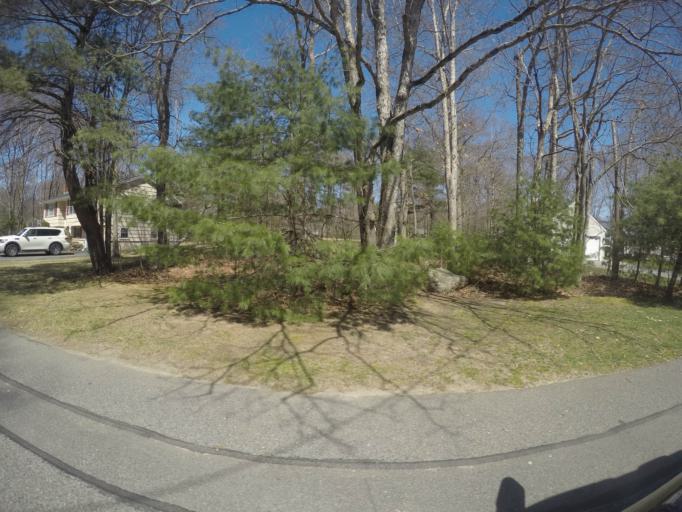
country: US
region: Massachusetts
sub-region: Bristol County
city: Easton
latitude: 42.0374
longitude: -71.0912
